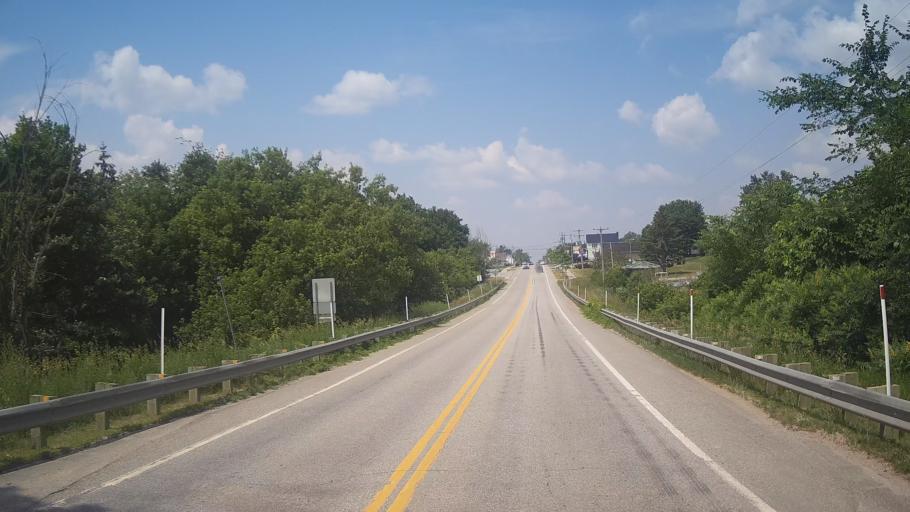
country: CA
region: Quebec
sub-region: Outaouais
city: Shawville
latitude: 45.5977
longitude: -76.4883
